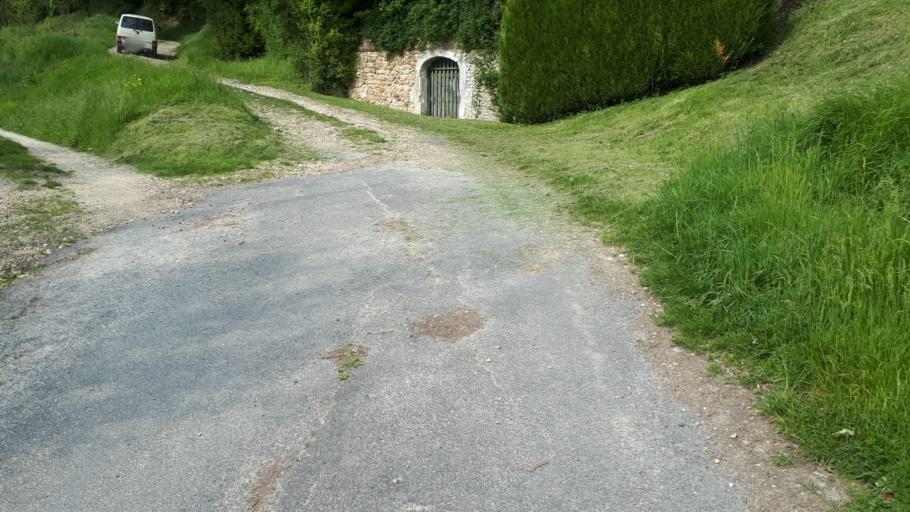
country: FR
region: Centre
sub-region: Departement du Loir-et-Cher
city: Lunay
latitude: 47.8338
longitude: 0.9382
